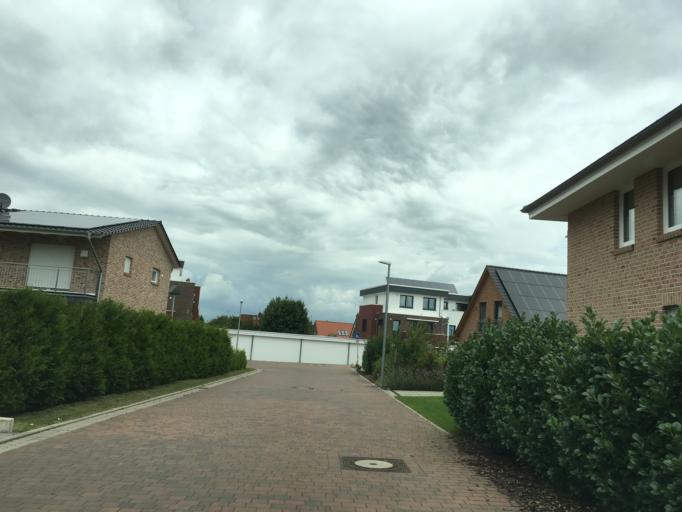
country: DE
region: Lower Saxony
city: Embsen
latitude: 53.2097
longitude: 10.3715
